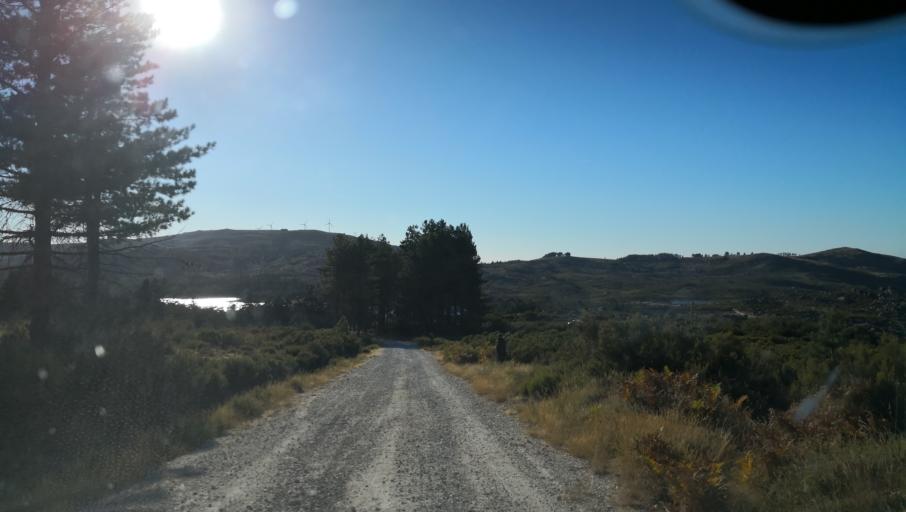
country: PT
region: Vila Real
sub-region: Vila Real
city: Vila Real
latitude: 41.3554
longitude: -7.7846
